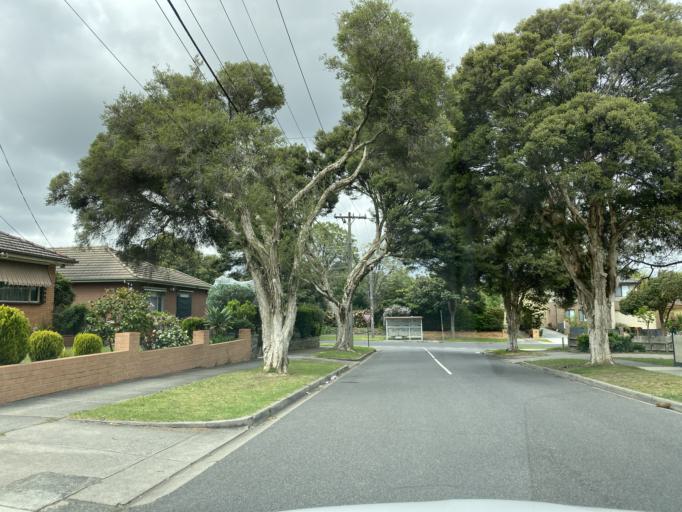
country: AU
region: Victoria
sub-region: Whitehorse
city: Burwood
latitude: -37.8445
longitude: 145.1262
